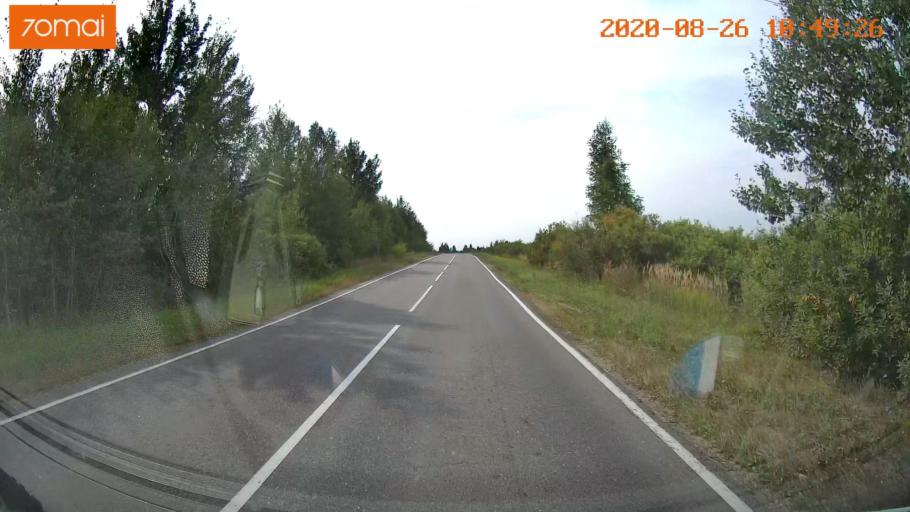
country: RU
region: Rjazan
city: Lashma
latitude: 54.7026
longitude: 41.1600
